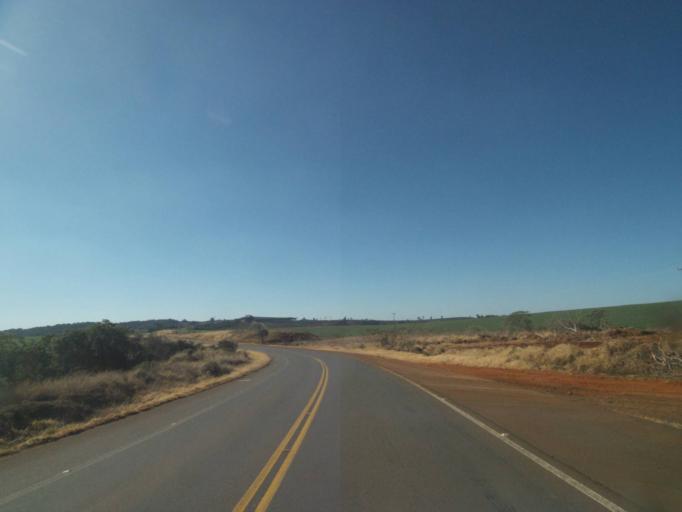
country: BR
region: Parana
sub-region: Tibagi
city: Tibagi
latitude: -24.7473
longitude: -50.4620
